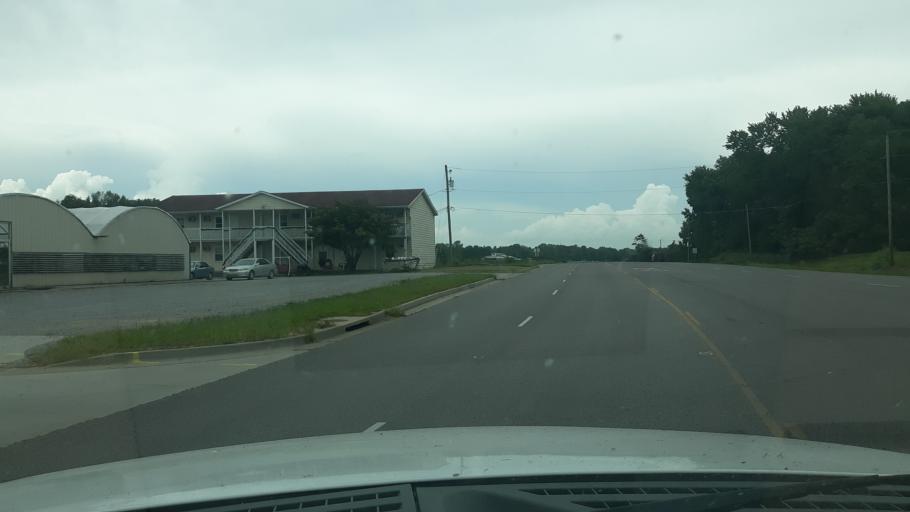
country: US
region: Illinois
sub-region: Saline County
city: Eldorado
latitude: 37.8124
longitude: -88.4270
